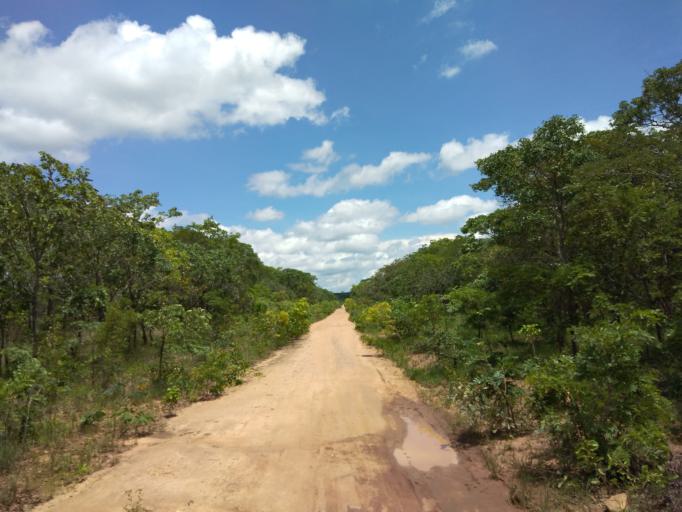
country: ZM
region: Central
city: Mkushi
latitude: -13.9580
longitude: 29.9122
